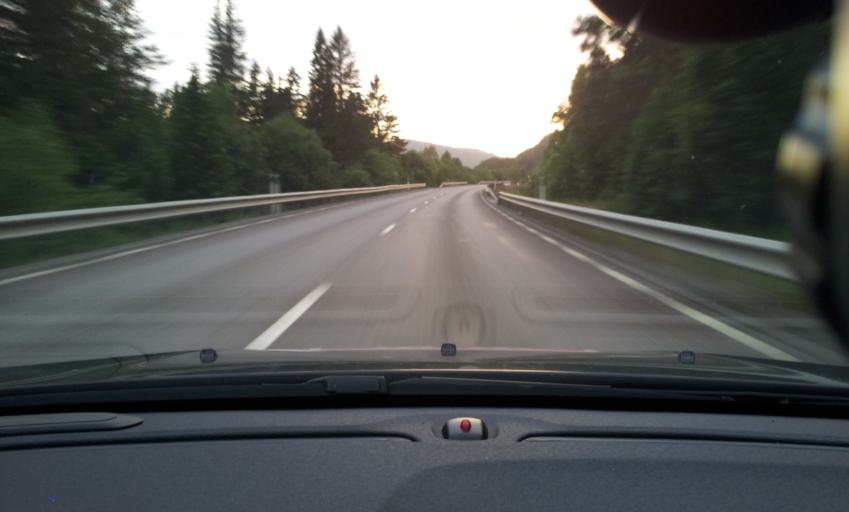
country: SE
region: Jaemtland
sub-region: Ragunda Kommun
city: Hammarstrand
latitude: 63.0934
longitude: 16.4111
